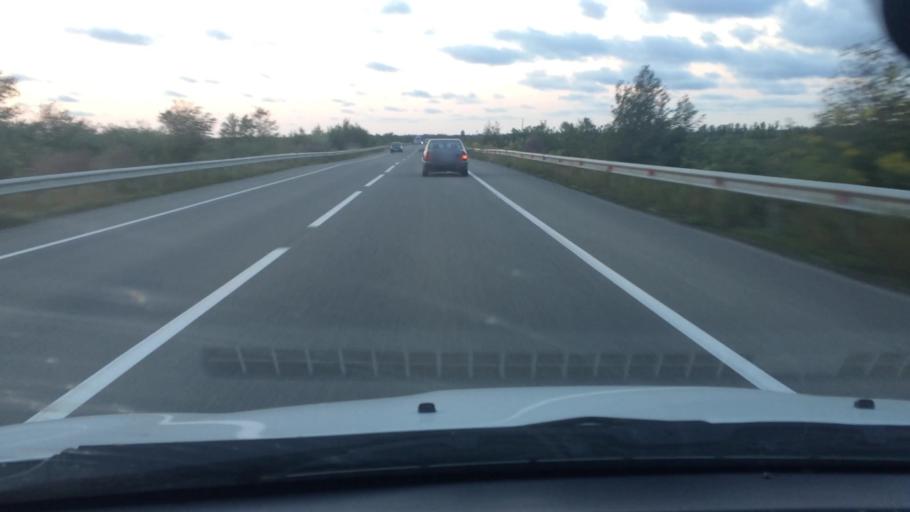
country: GE
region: Ajaria
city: Ochkhamuri
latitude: 41.9048
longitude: 41.7895
